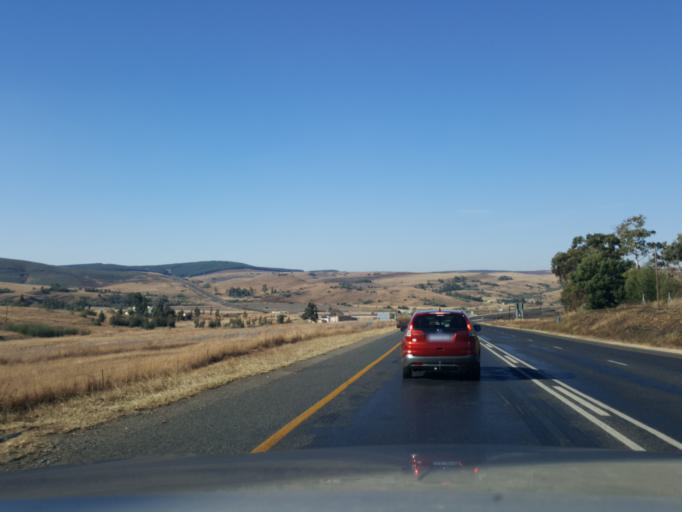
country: ZA
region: Mpumalanga
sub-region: Nkangala District Municipality
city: Belfast
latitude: -25.6136
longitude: 30.2714
